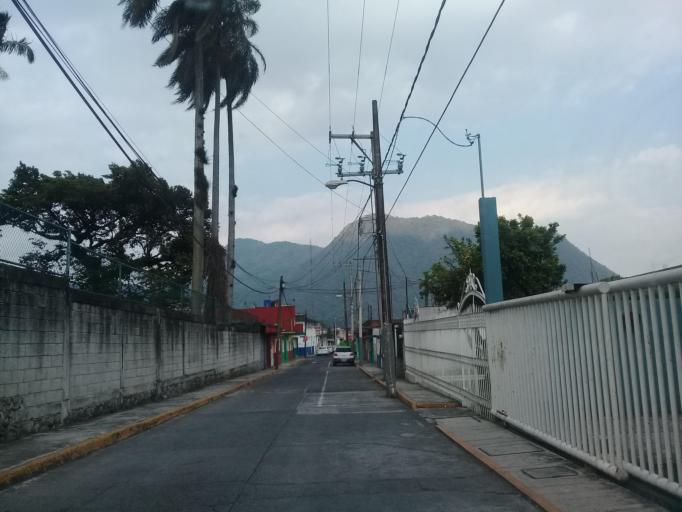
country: MX
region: Veracruz
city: Orizaba
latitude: 18.8597
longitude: -97.1071
